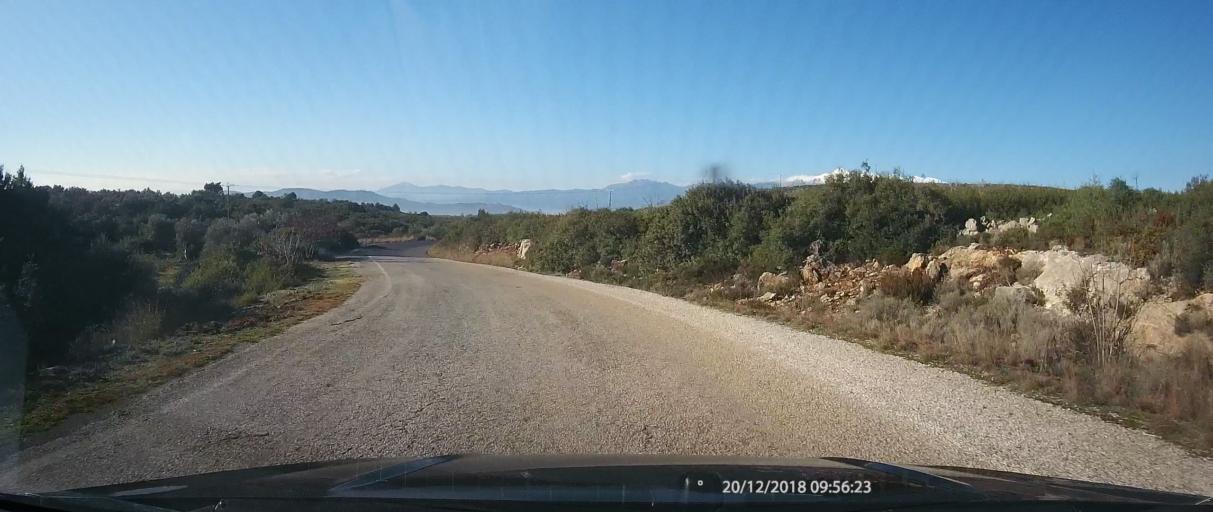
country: GR
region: Peloponnese
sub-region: Nomos Lakonias
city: Yerakion
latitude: 37.0225
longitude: 22.6125
